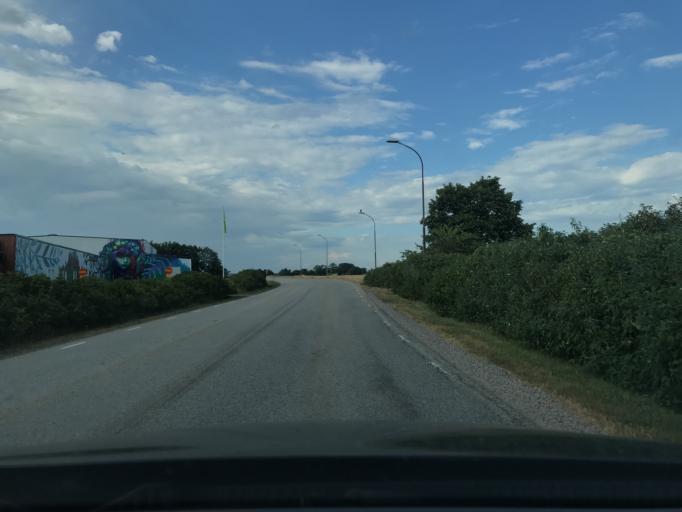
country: SE
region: Skane
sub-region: Simrishamns Kommun
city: Kivik
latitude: 55.5076
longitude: 14.1529
